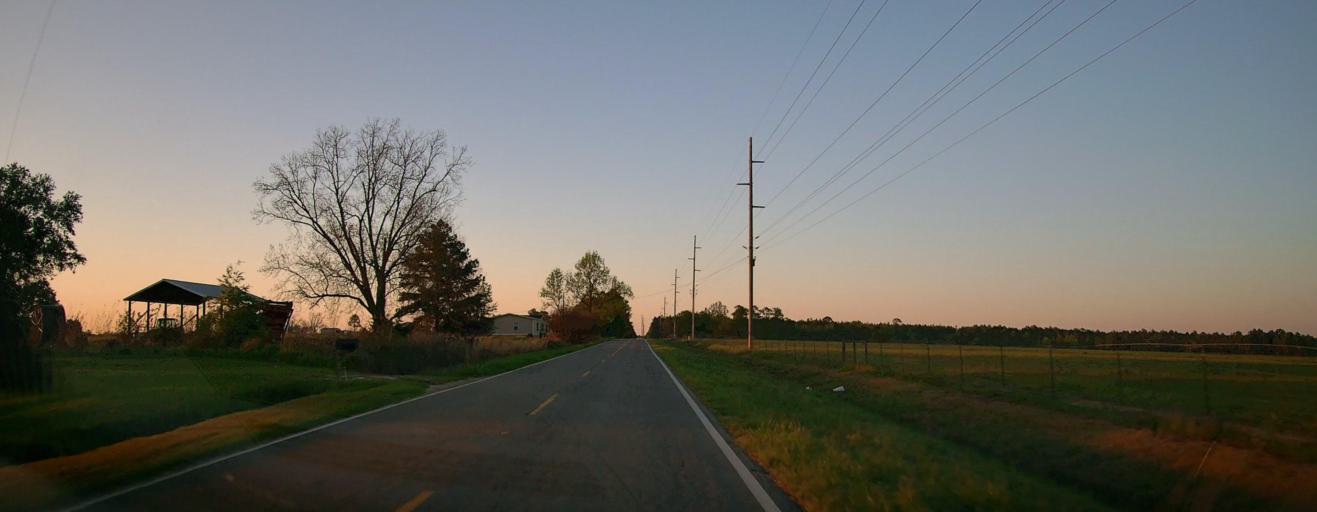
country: US
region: Georgia
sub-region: Ben Hill County
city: Fitzgerald
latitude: 31.7648
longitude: -83.3550
